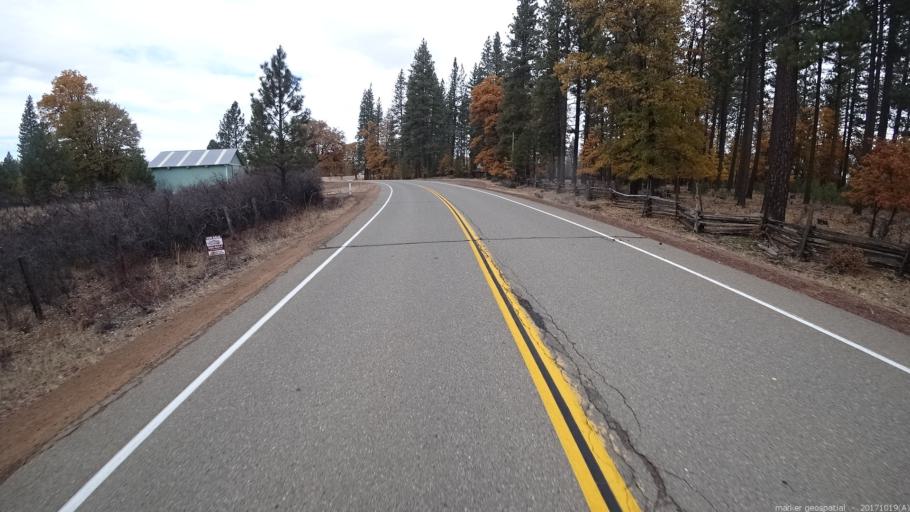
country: US
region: California
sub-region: Shasta County
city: Burney
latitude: 41.1083
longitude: -121.5621
